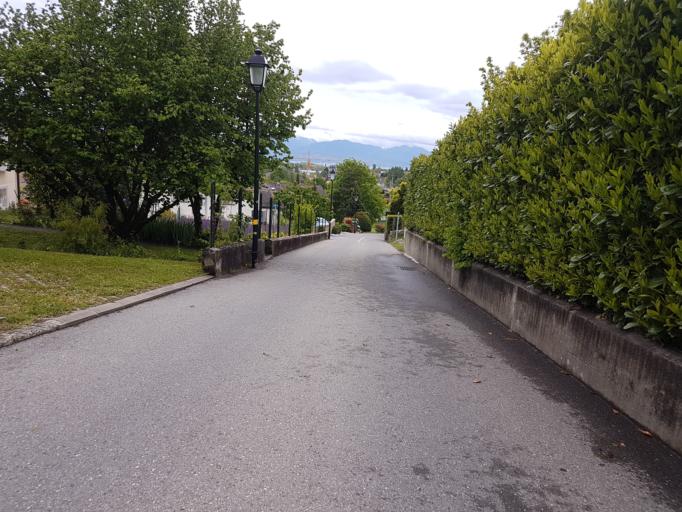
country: CH
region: Vaud
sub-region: Morges District
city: Preverenges
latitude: 46.5320
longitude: 6.5422
